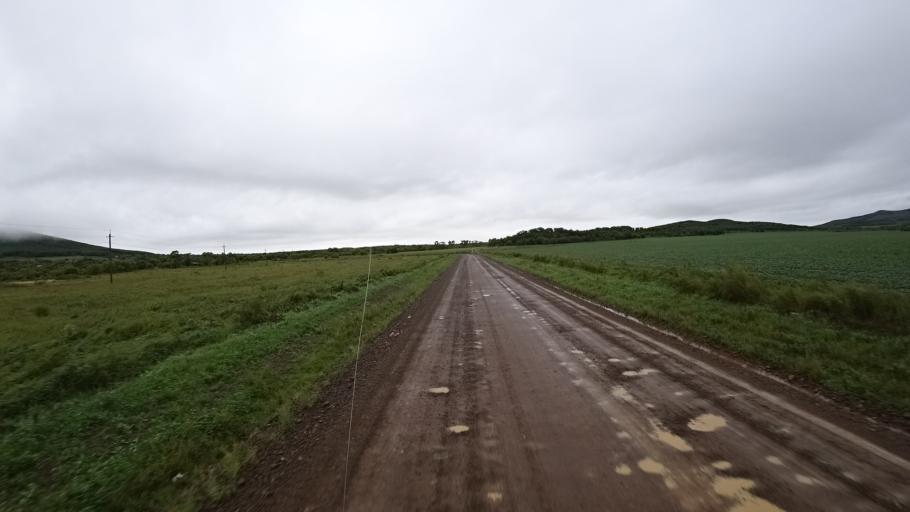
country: RU
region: Primorskiy
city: Monastyrishche
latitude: 44.2532
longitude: 132.4331
